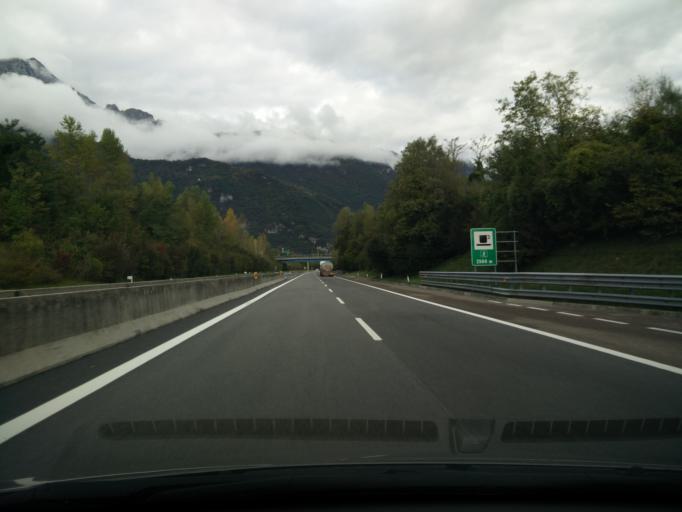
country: IT
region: Veneto
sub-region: Provincia di Belluno
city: Soccher-Paiane-Casan-Arsie
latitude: 46.1797
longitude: 12.2974
